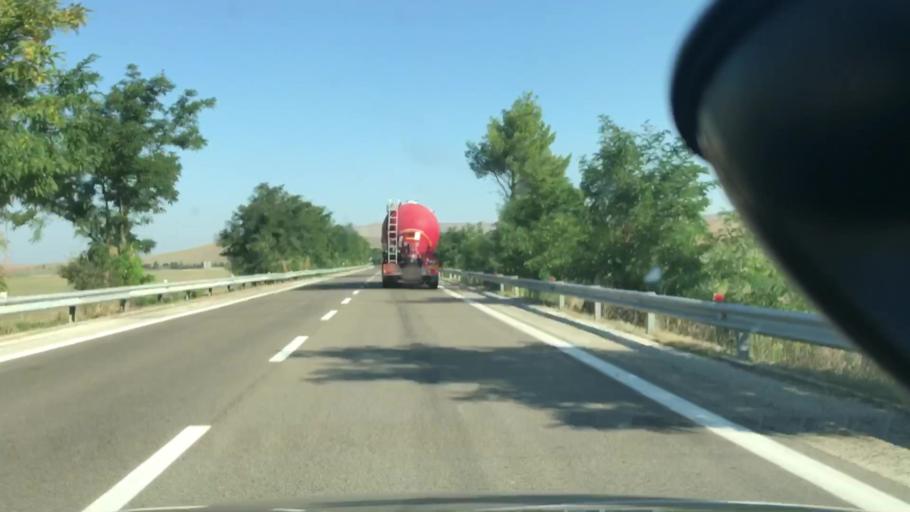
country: IT
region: Basilicate
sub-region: Provincia di Matera
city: Irsina
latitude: 40.8003
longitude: 16.2745
